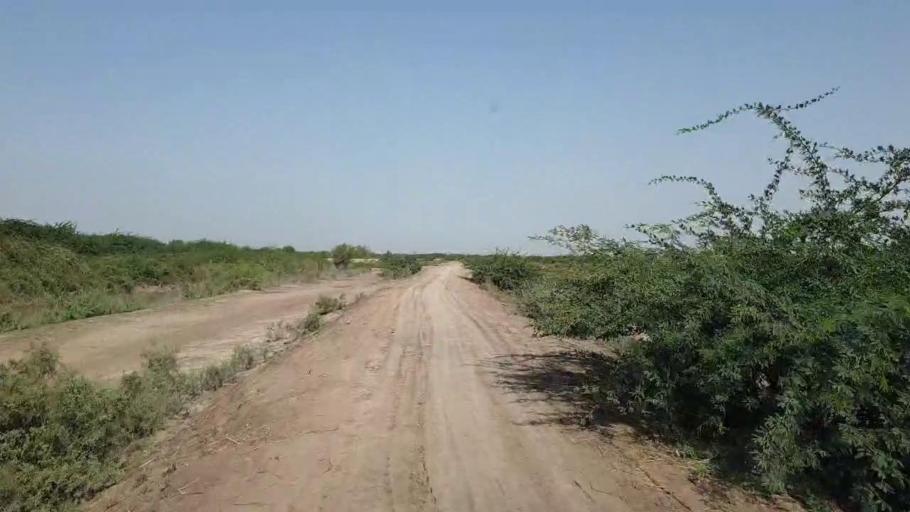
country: PK
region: Sindh
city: Tando Bago
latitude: 24.6548
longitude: 69.0704
